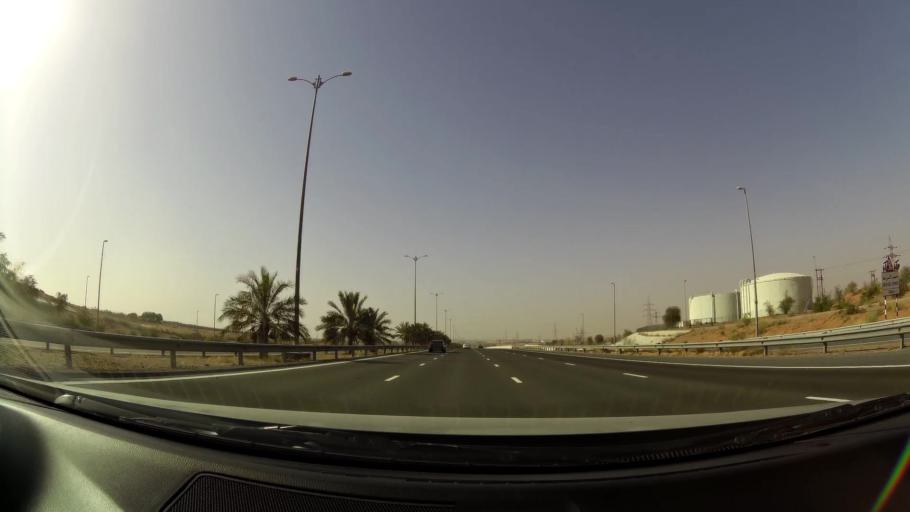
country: OM
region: Al Buraimi
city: Al Buraymi
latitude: 24.4885
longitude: 55.7721
